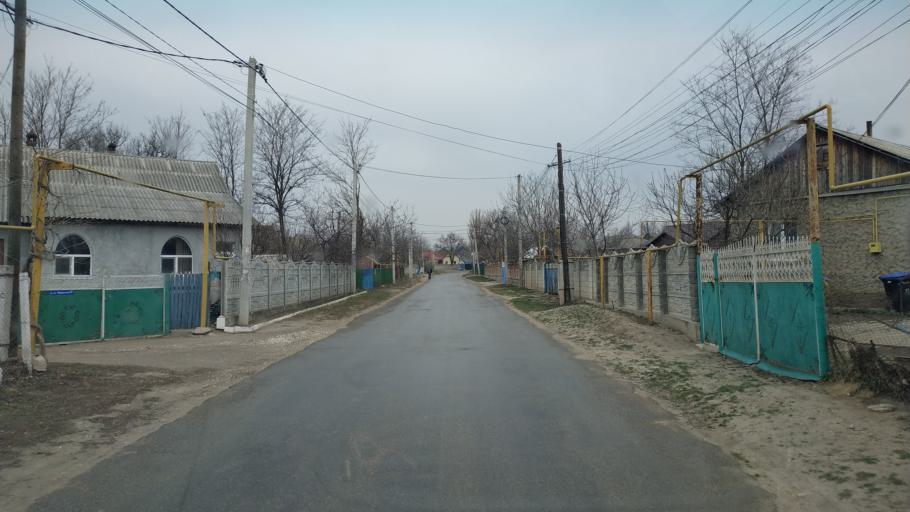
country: MD
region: Chisinau
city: Singera
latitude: 46.9075
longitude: 28.9457
